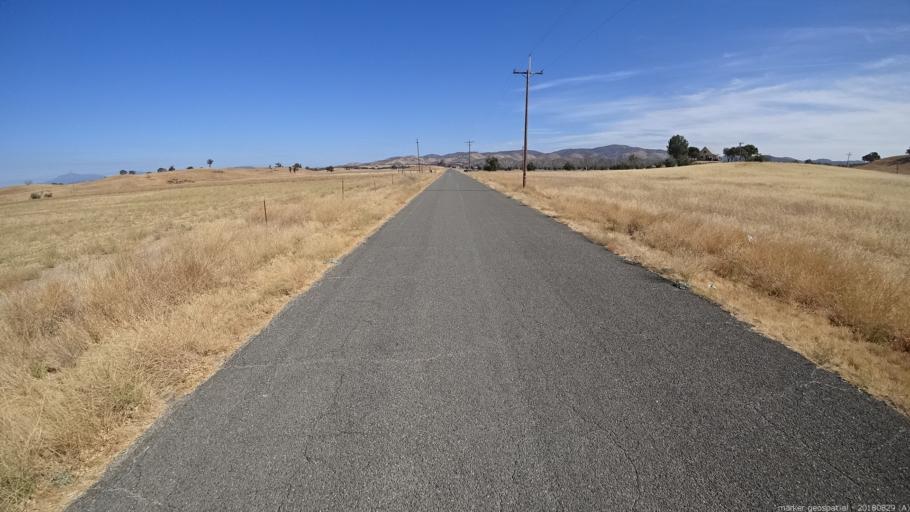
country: US
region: California
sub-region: Monterey County
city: King City
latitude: 35.9506
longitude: -121.1176
